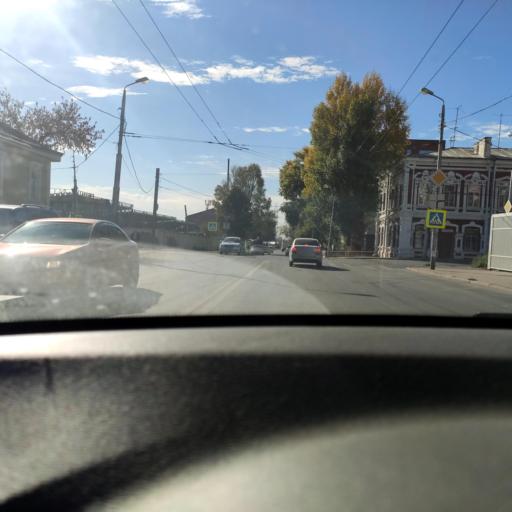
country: RU
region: Samara
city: Samara
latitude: 53.1841
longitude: 50.1069
